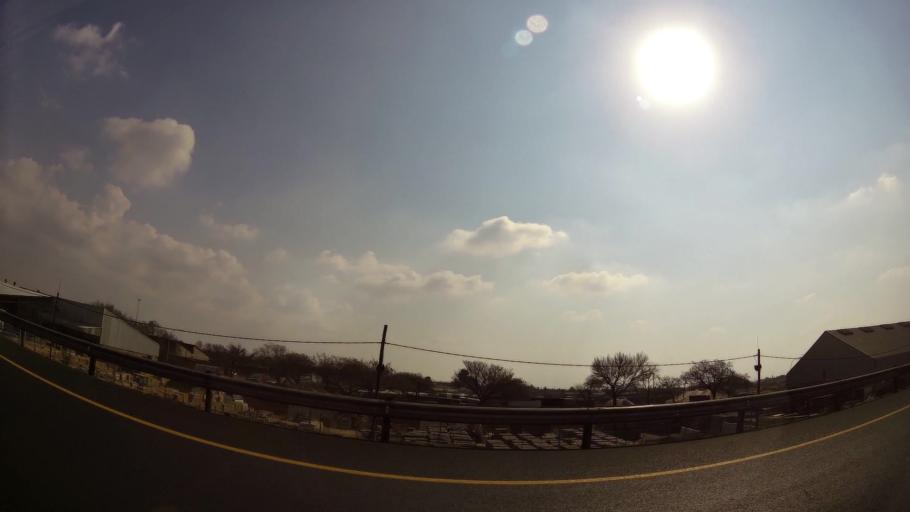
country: ZA
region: Gauteng
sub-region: Ekurhuleni Metropolitan Municipality
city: Brakpan
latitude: -26.1580
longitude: 28.4213
